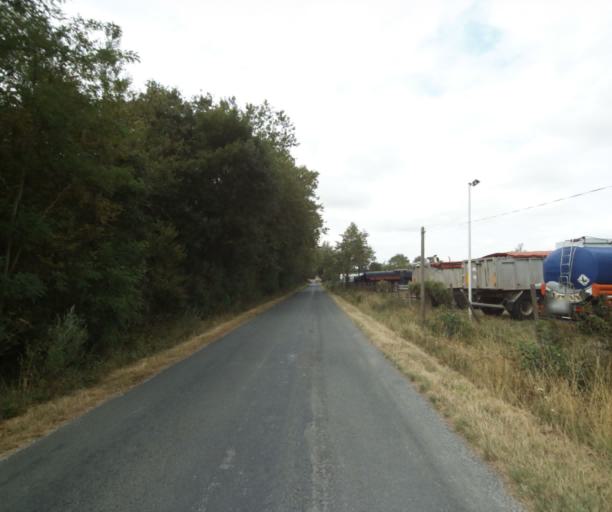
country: FR
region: Midi-Pyrenees
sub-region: Departement du Tarn
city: Soreze
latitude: 43.4494
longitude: 2.0506
